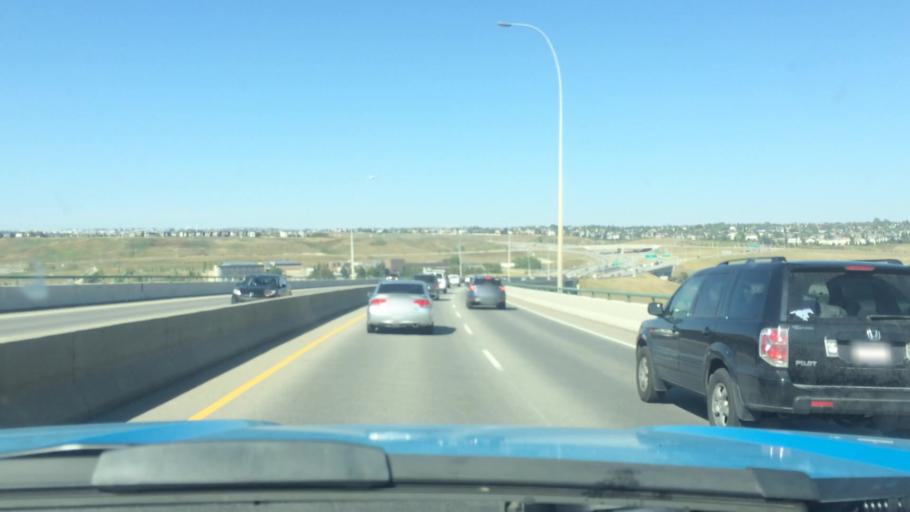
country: CA
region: Alberta
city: Calgary
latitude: 51.0967
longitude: -114.2330
